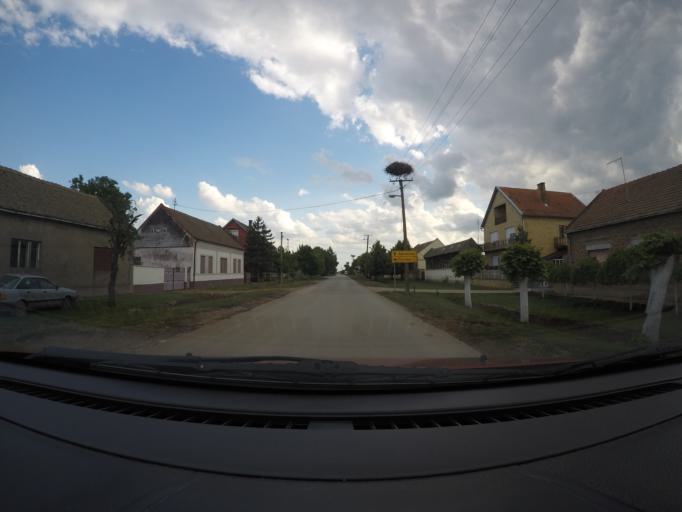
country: RS
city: Tomasevac
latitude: 45.2630
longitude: 20.6183
